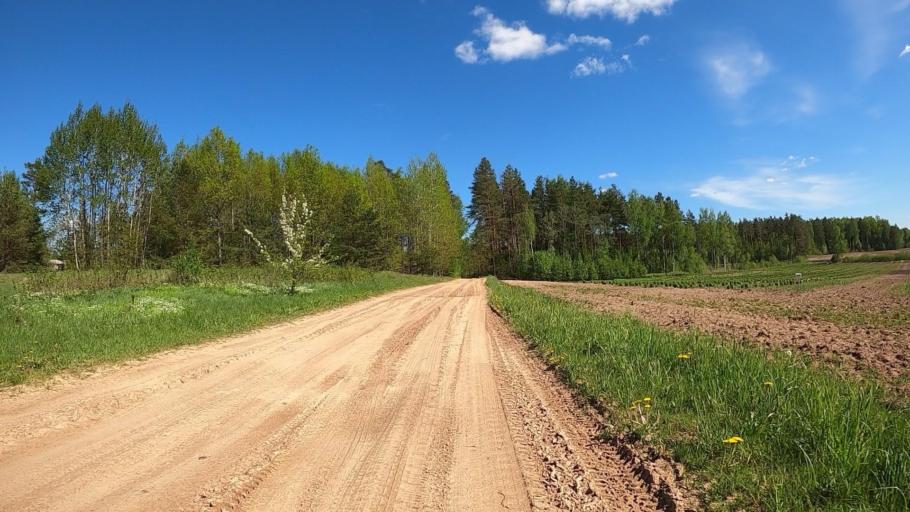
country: LV
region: Salaspils
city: Salaspils
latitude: 56.7909
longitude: 24.3175
